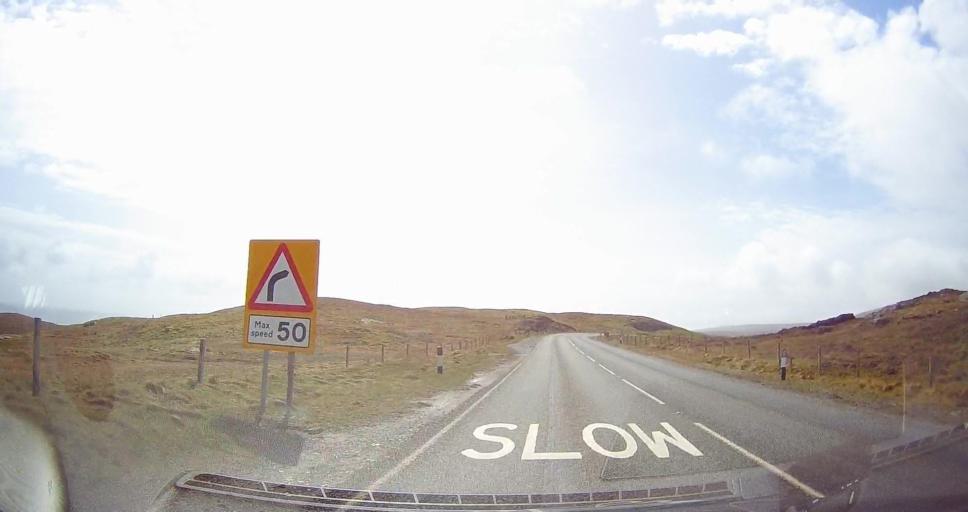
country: GB
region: Scotland
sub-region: Shetland Islands
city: Lerwick
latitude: 60.1085
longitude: -1.2195
